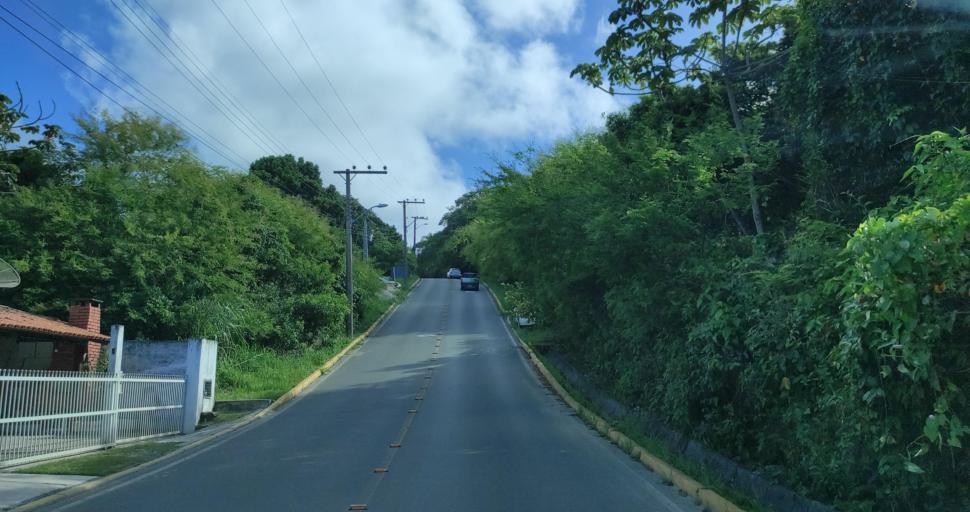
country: BR
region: Santa Catarina
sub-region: Porto Belo
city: Porto Belo
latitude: -27.1535
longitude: -48.4916
